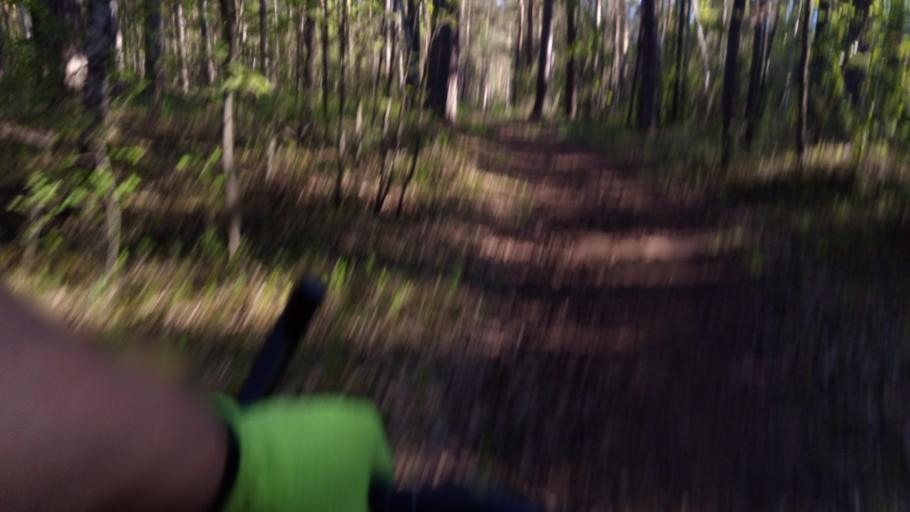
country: RU
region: Chelyabinsk
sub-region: Gorod Chelyabinsk
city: Chelyabinsk
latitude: 55.1326
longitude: 61.3360
